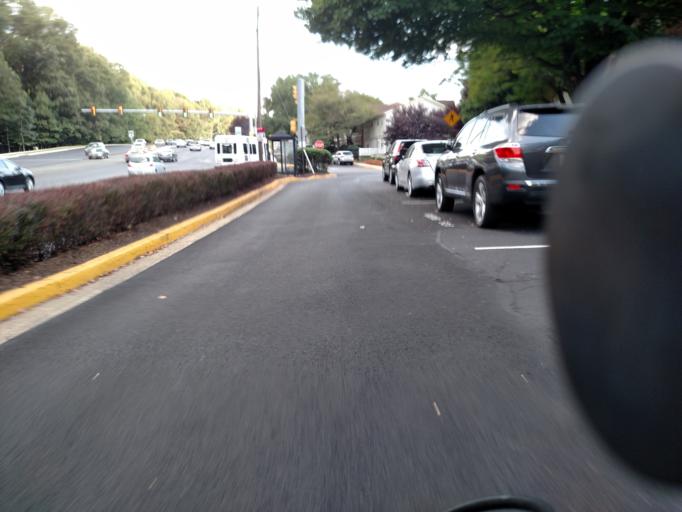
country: US
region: Virginia
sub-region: Fairfax County
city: Merrifield
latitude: 38.8617
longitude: -77.2277
